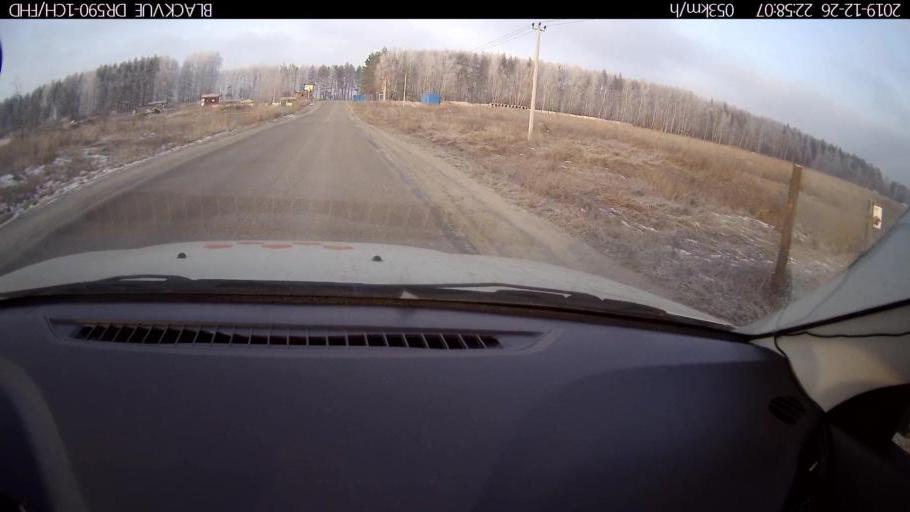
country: RU
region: Nizjnij Novgorod
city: Burevestnik
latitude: 56.1557
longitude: 43.7100
